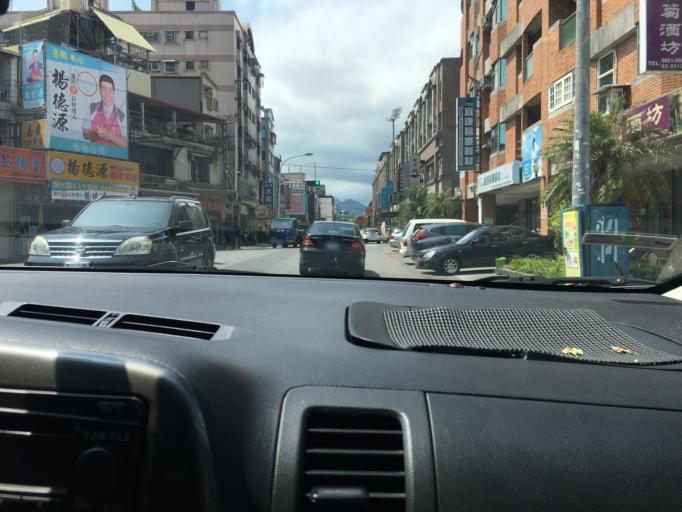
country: TW
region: Taiwan
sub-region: Yilan
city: Yilan
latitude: 24.7448
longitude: 121.7500
